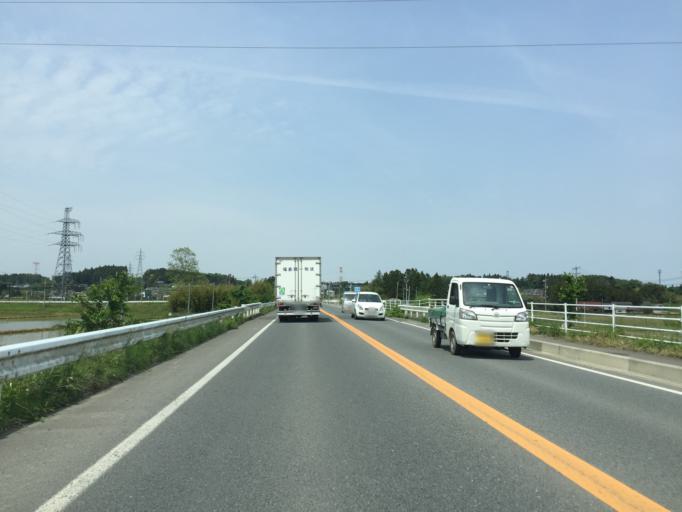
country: JP
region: Miyagi
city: Marumori
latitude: 37.8297
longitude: 140.9186
